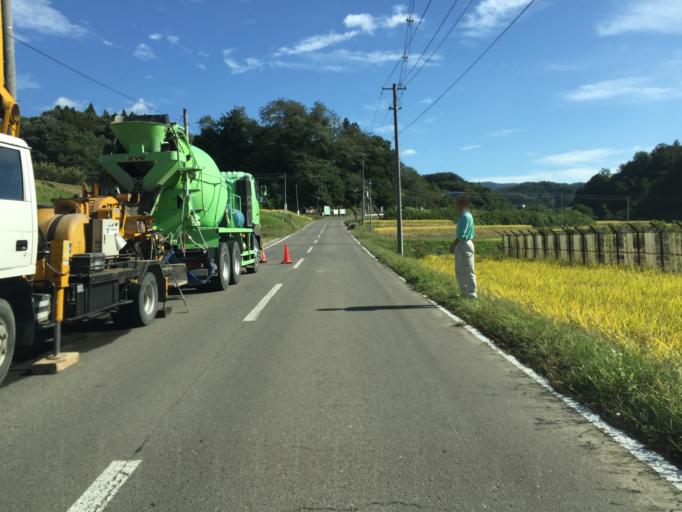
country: JP
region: Fukushima
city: Yanagawamachi-saiwaicho
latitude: 37.8503
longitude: 140.6517
